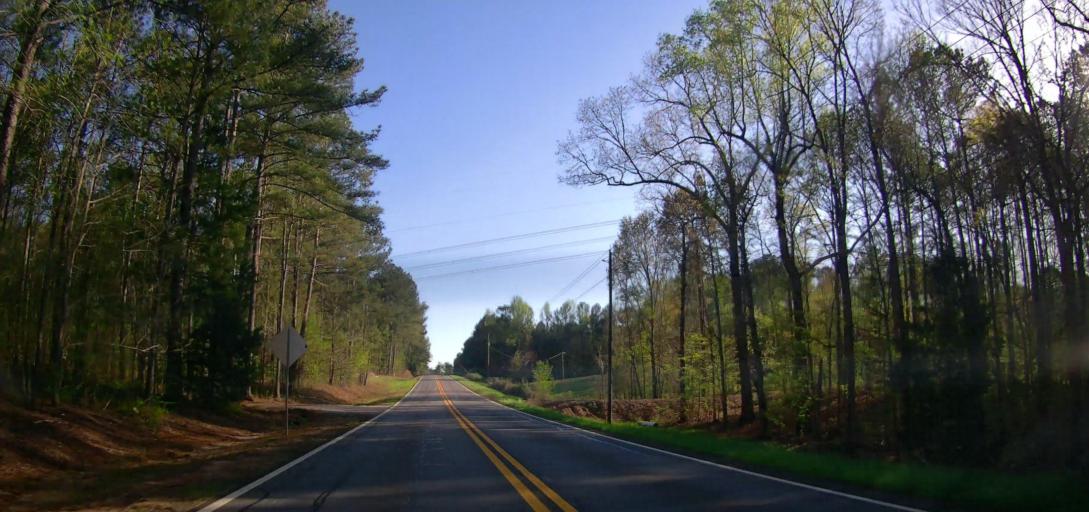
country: US
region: Georgia
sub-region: Monroe County
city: Forsyth
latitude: 33.1165
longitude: -83.9436
